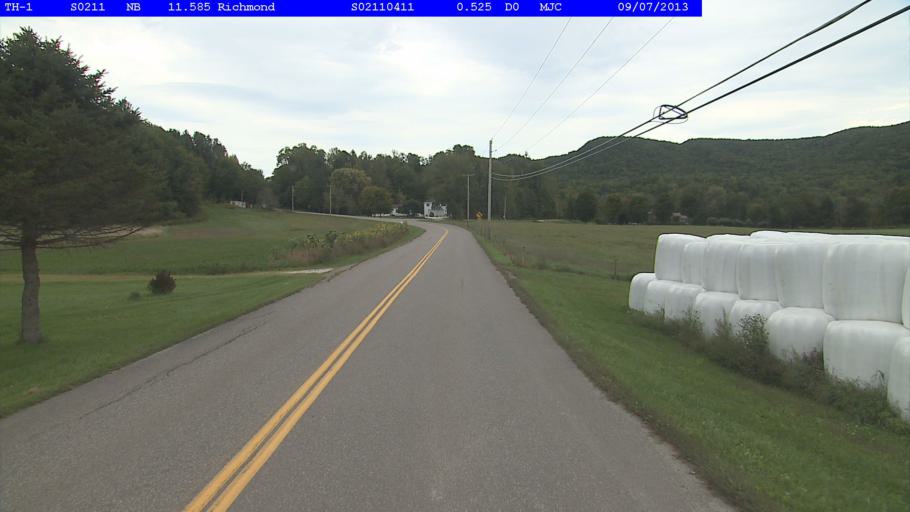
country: US
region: Vermont
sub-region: Chittenden County
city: Williston
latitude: 44.3608
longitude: -72.9934
